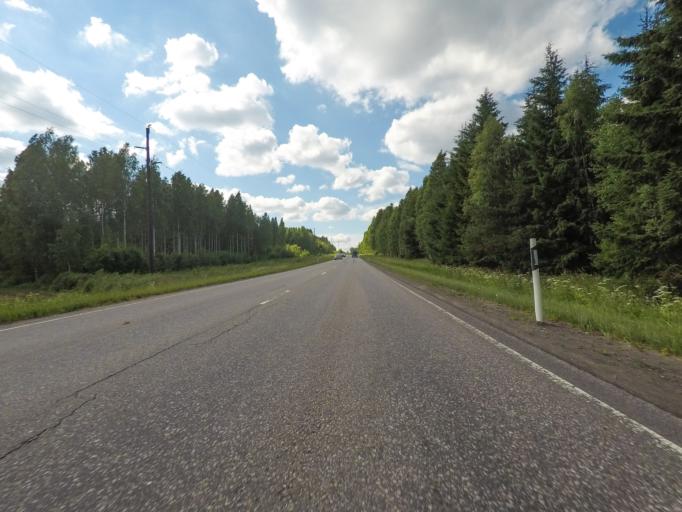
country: FI
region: Southern Savonia
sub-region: Savonlinna
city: Kerimaeki
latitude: 61.8418
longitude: 29.2068
